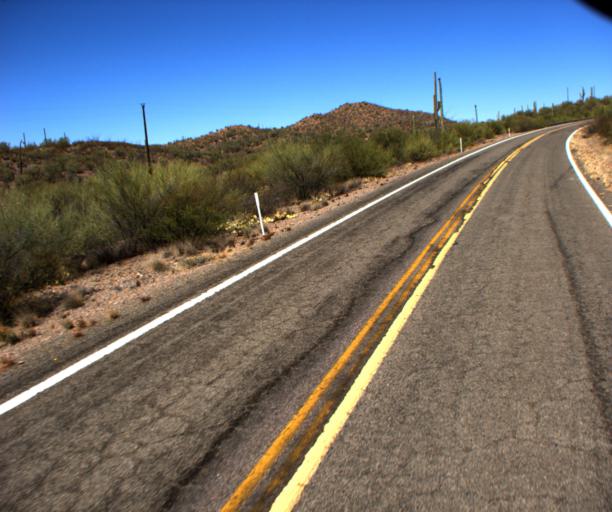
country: US
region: Arizona
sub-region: Pima County
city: Sells
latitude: 32.1741
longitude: -112.1655
